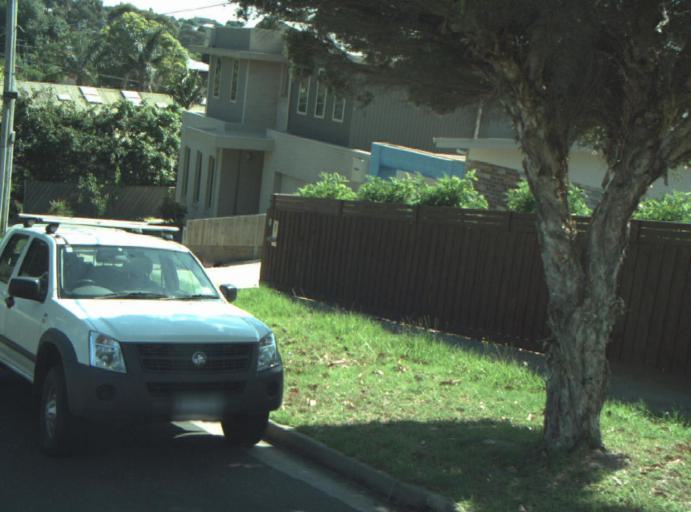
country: AU
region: Victoria
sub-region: Greater Geelong
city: Wandana Heights
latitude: -38.1709
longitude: 144.3140
